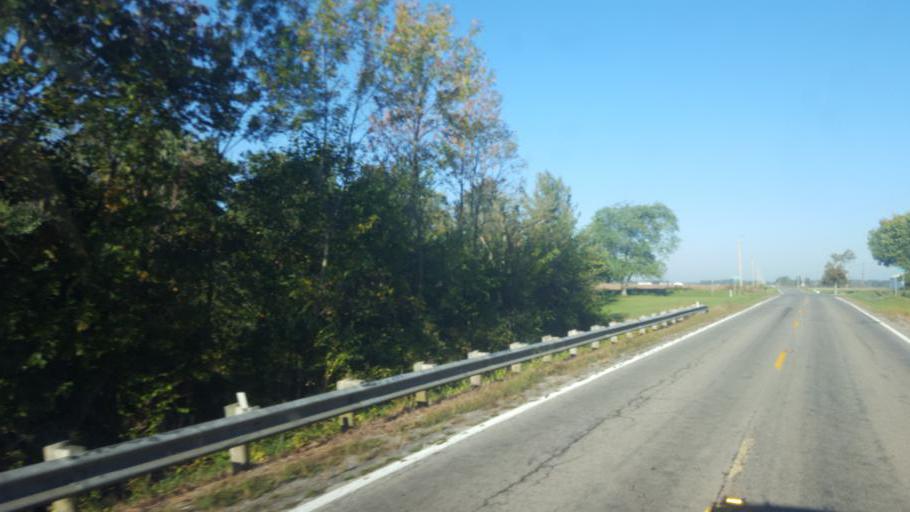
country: US
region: Ohio
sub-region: Marion County
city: Marion
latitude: 40.5443
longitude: -83.0196
